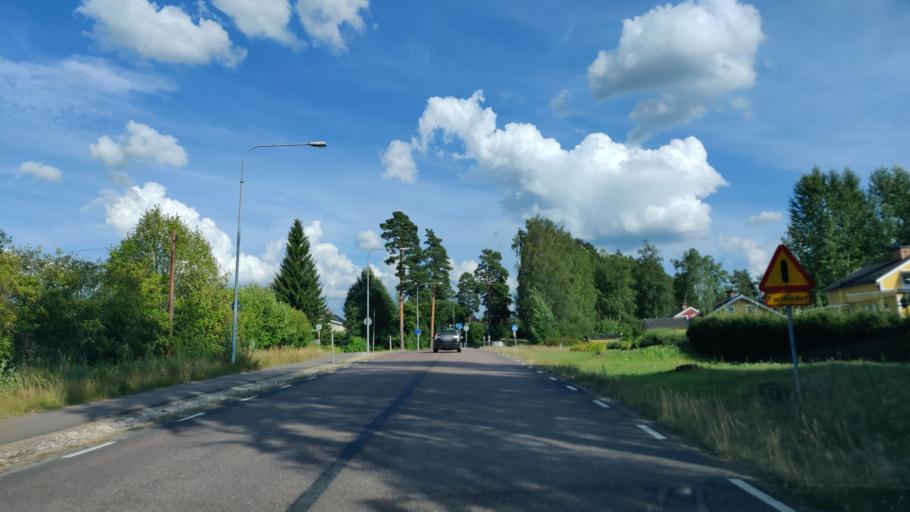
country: SE
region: Vaermland
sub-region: Hagfors Kommun
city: Hagfors
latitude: 60.0435
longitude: 13.6852
